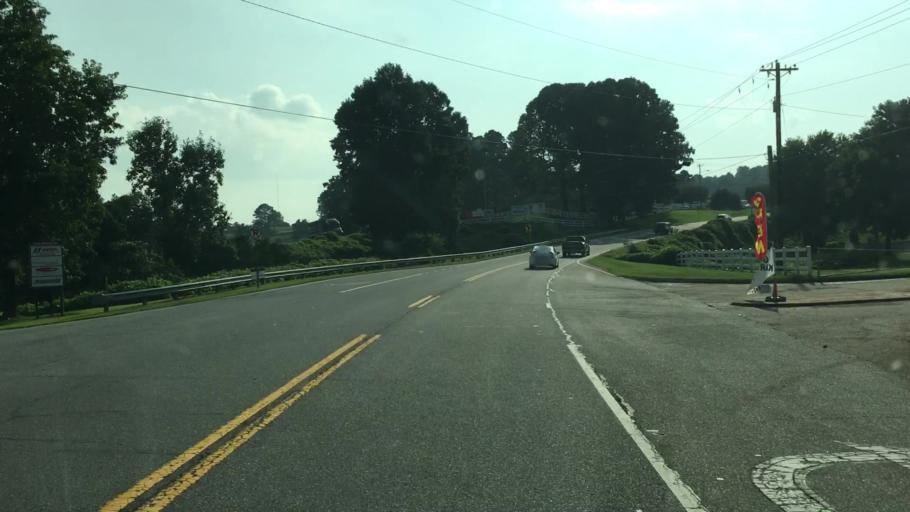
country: US
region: Georgia
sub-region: Jackson County
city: Braselton
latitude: 34.1519
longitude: -83.8107
